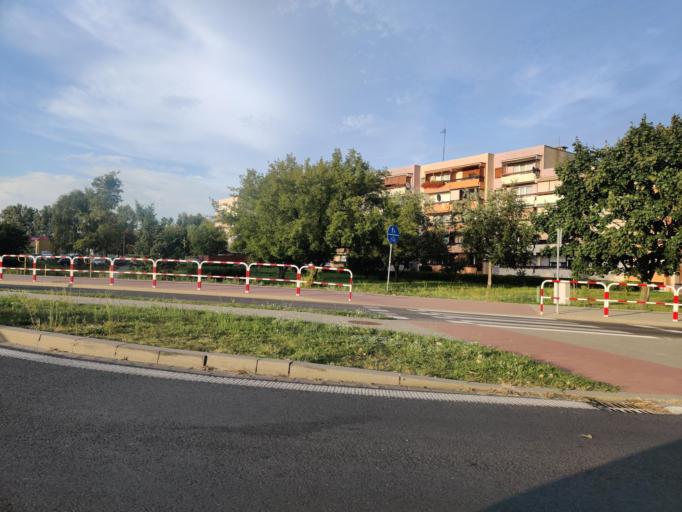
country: PL
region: Greater Poland Voivodeship
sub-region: Konin
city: Konin
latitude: 52.2342
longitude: 18.2467
